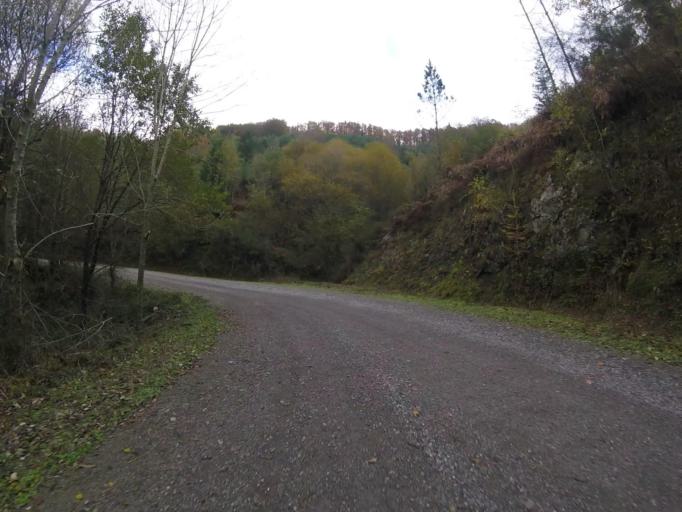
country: ES
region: Navarre
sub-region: Provincia de Navarra
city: Goizueta
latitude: 43.2213
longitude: -1.8284
